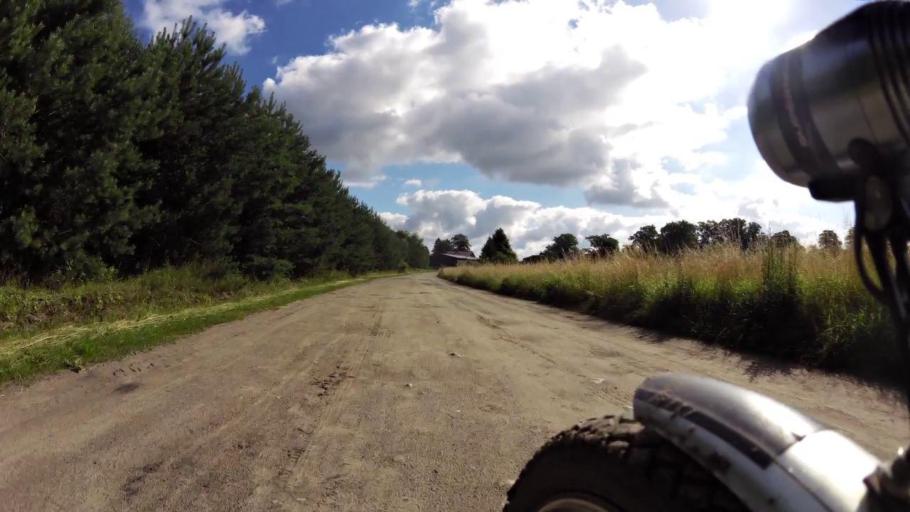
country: PL
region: West Pomeranian Voivodeship
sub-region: Powiat swidwinski
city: Rabino
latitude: 53.7568
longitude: 15.9086
